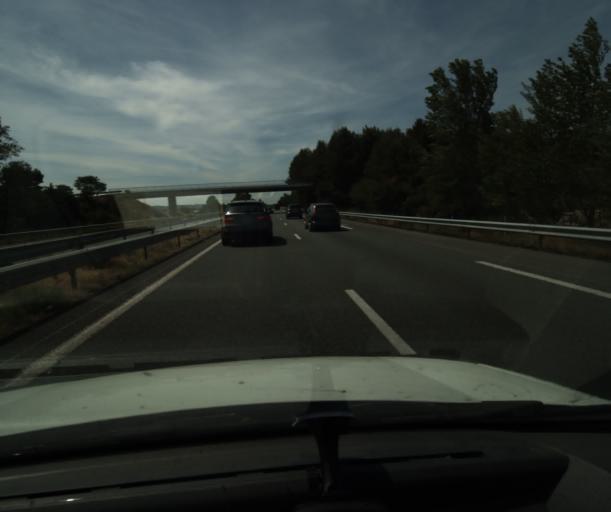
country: FR
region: Languedoc-Roussillon
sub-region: Departement de l'Aude
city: Saint-Martin-Lalande
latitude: 43.2538
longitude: 2.0430
